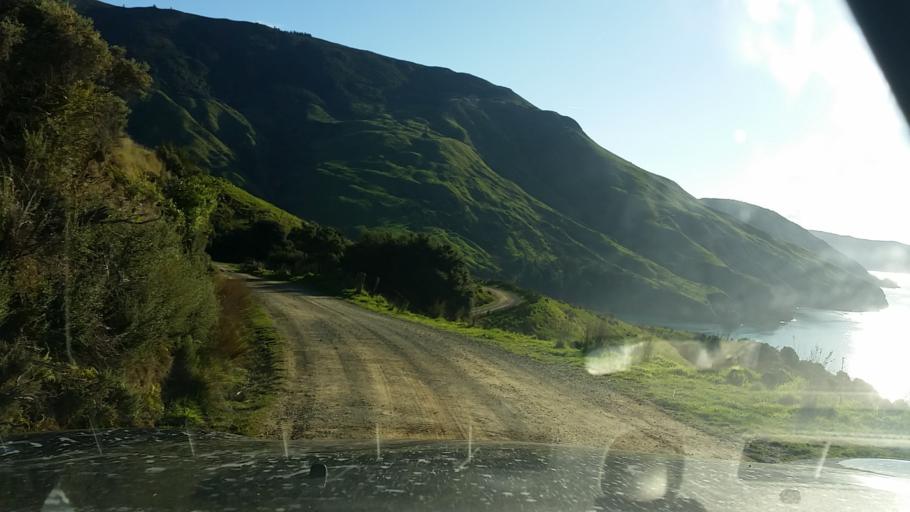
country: NZ
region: Marlborough
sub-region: Marlborough District
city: Picton
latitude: -41.0218
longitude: 174.1423
